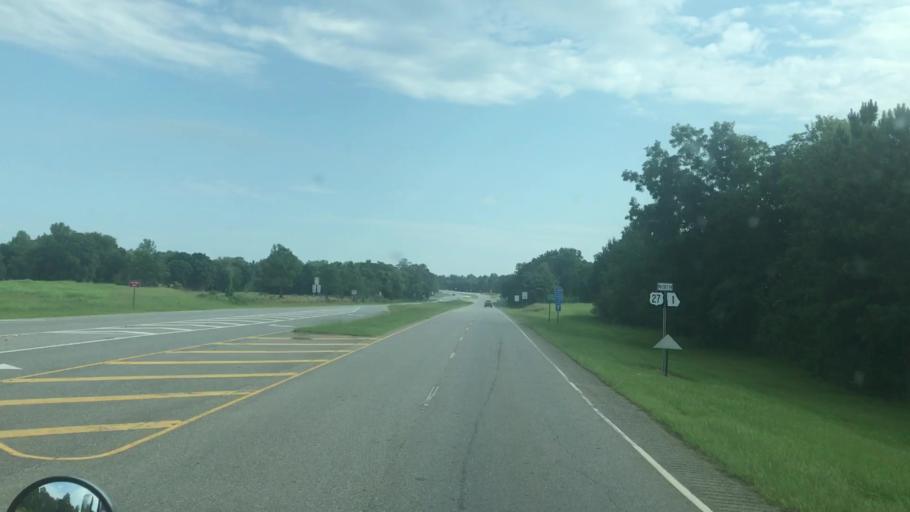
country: US
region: Georgia
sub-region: Early County
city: Blakely
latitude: 31.3756
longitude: -84.9215
